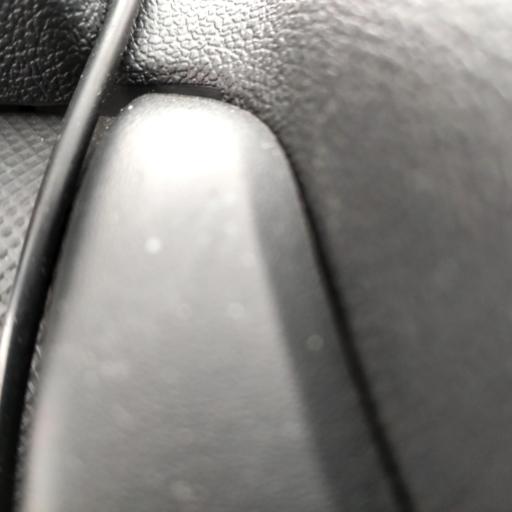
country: RU
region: Voronezj
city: Ostrogozhsk
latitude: 50.8425
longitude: 39.0316
